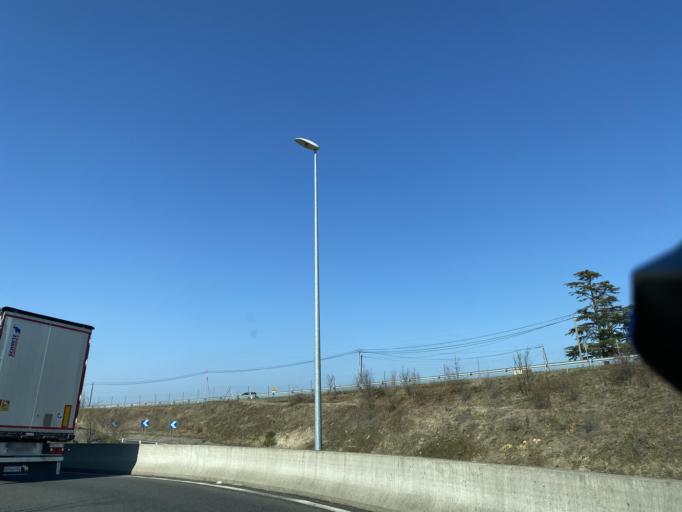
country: FR
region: Rhone-Alpes
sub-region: Departement du Rhone
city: Saint-Germain-Nuelles
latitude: 45.8658
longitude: 4.5975
